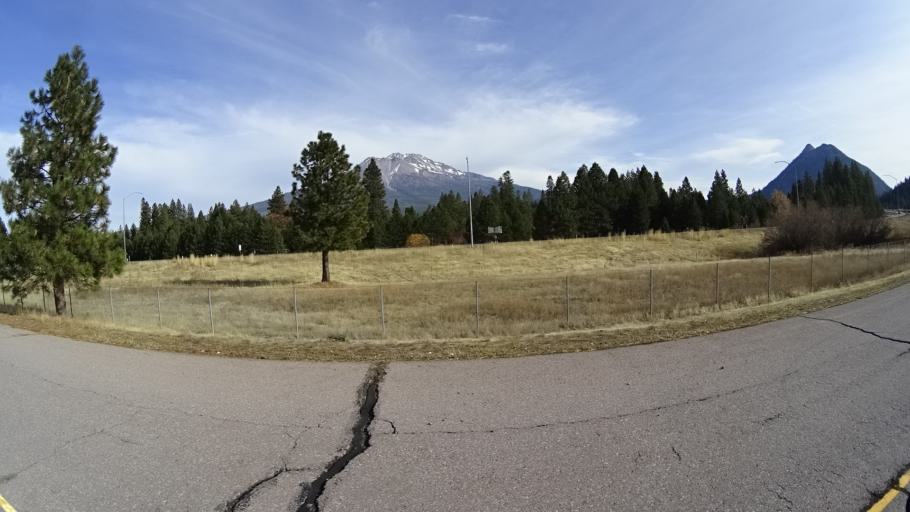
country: US
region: California
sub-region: Siskiyou County
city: Weed
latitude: 41.4018
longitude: -122.3842
